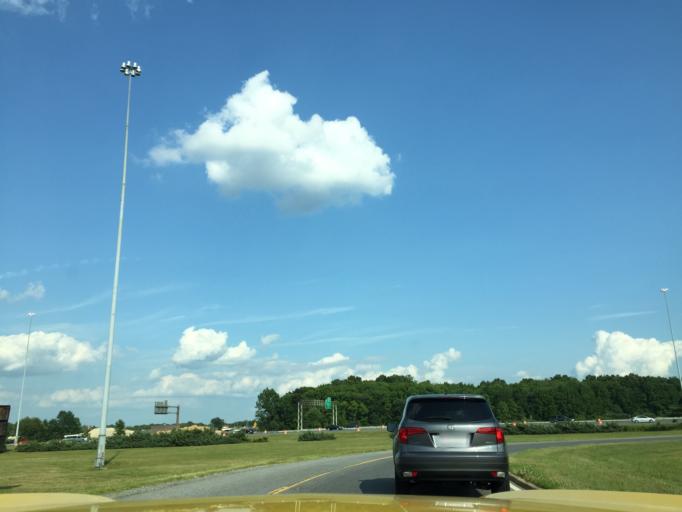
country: US
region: Delaware
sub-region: New Castle County
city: Bear
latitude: 39.6744
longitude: -75.6751
